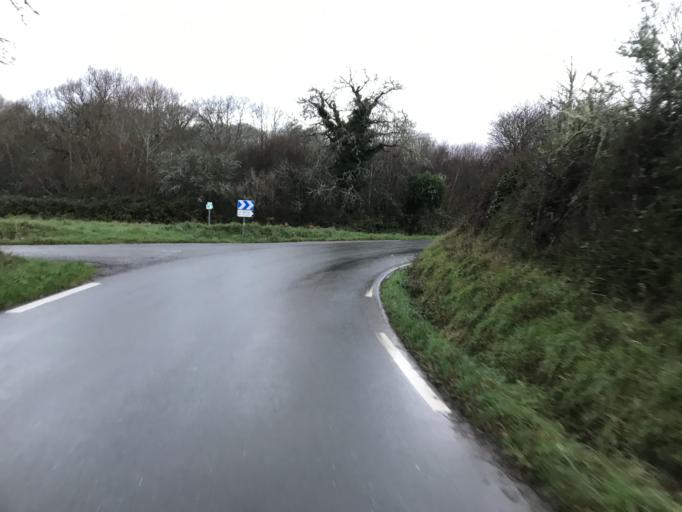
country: FR
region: Brittany
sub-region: Departement du Finistere
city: Plougastel-Daoulas
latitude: 48.3588
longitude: -4.3490
